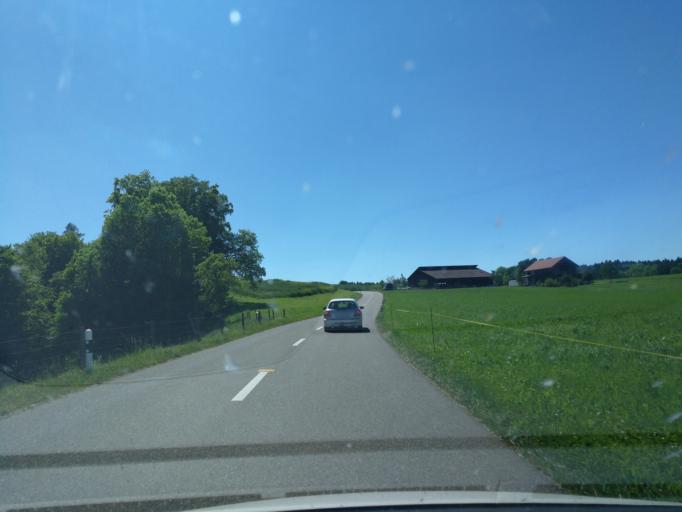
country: CH
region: Thurgau
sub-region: Weinfelden District
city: Sulgen
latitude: 47.5102
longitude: 9.1689
